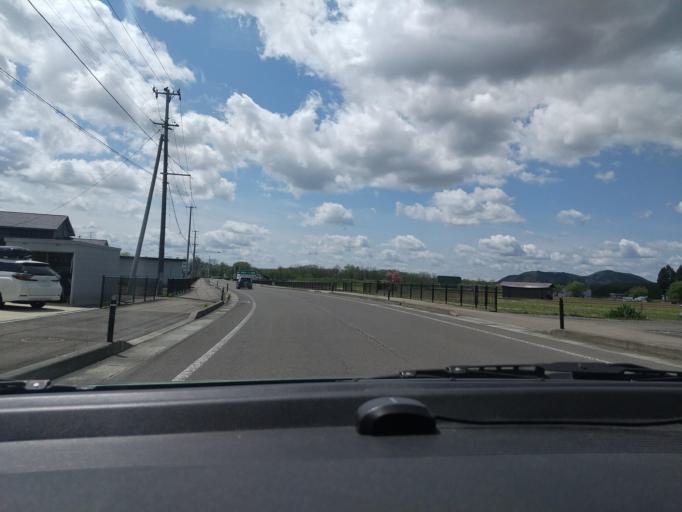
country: JP
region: Akita
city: Kakunodatemachi
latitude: 39.5897
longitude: 140.5588
